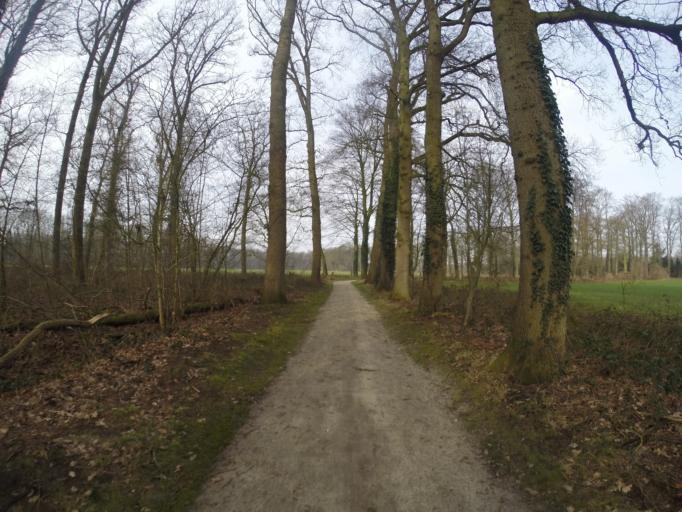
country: NL
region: Gelderland
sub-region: Gemeente Bronckhorst
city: Hengelo
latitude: 52.1017
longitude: 6.2936
